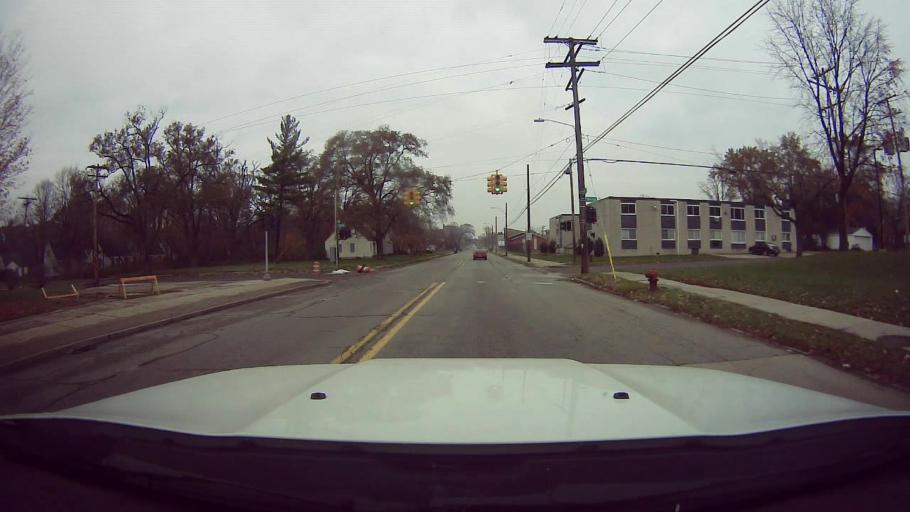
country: US
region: Michigan
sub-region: Wayne County
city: Redford
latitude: 42.4109
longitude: -83.2572
